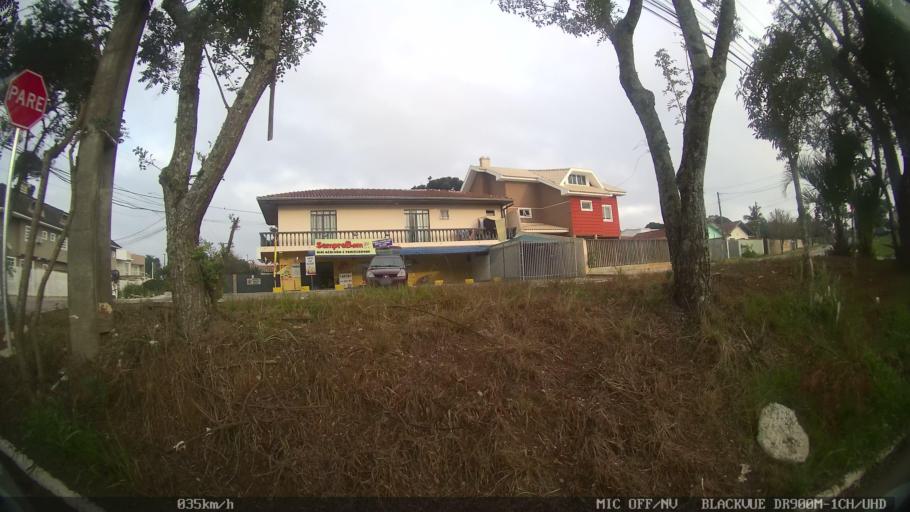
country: BR
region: Parana
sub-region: Almirante Tamandare
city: Almirante Tamandare
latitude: -25.3909
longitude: -49.3377
